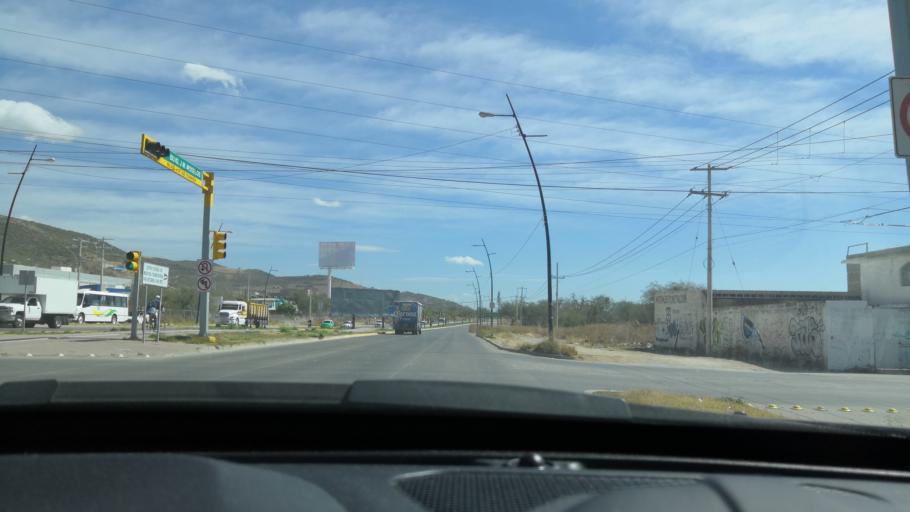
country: MX
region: Guanajuato
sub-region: Leon
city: Fraccionamiento Paraiso Real
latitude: 21.1248
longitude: -101.5963
